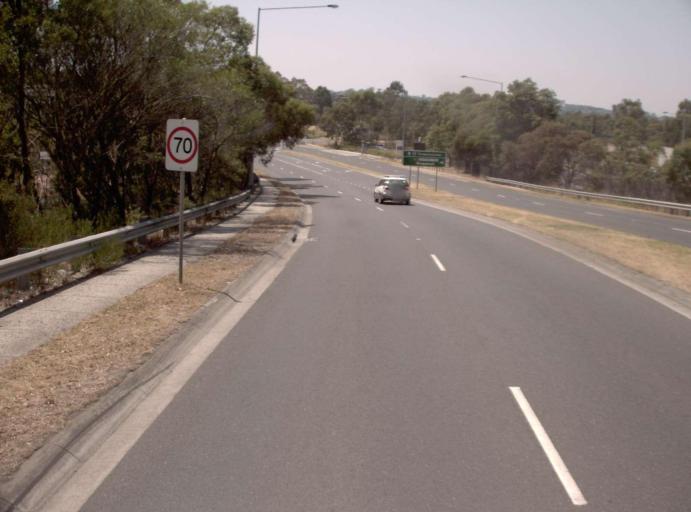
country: AU
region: Victoria
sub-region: Manningham
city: Bulleen
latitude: -37.7795
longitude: 145.0797
